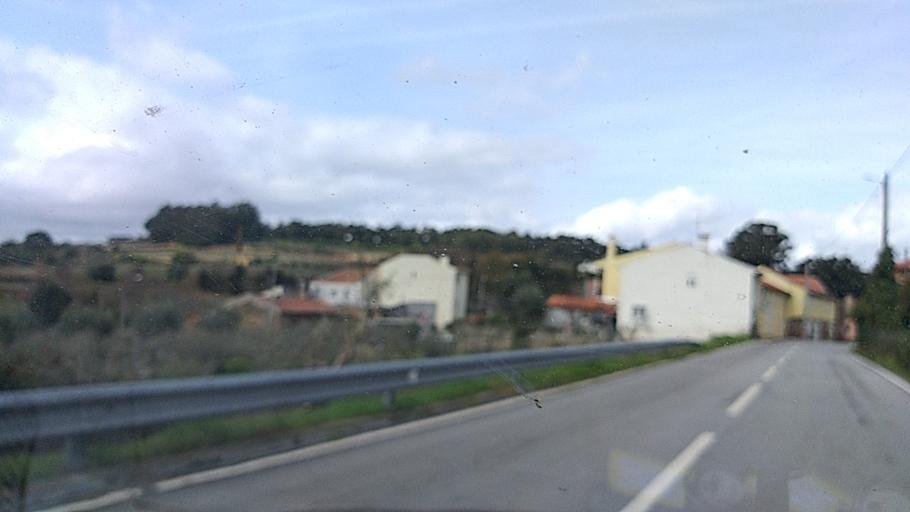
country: PT
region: Viseu
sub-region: Satao
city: Satao
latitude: 40.6684
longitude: -7.6927
